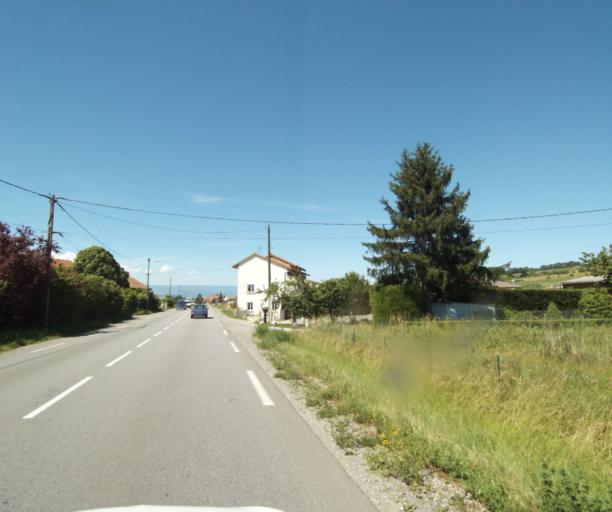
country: FR
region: Rhone-Alpes
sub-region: Departement de la Haute-Savoie
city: Loisin
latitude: 46.2836
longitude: 6.3093
